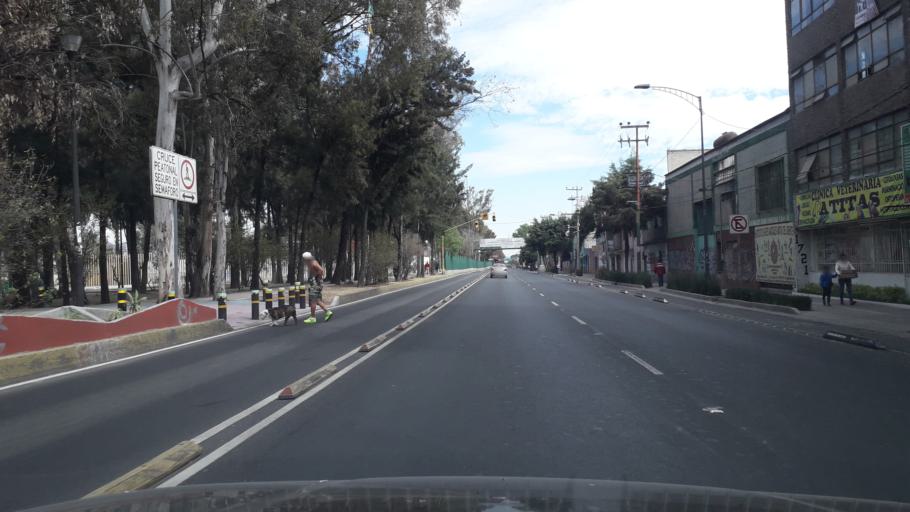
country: MX
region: Mexico City
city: Gustavo A. Madero
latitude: 19.4897
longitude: -99.0930
